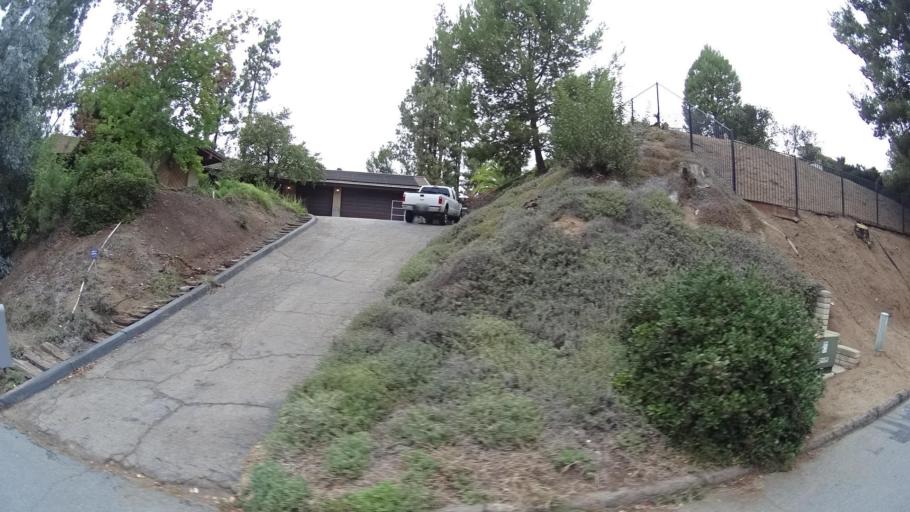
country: US
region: California
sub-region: San Diego County
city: Granite Hills
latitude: 32.7743
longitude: -116.9162
